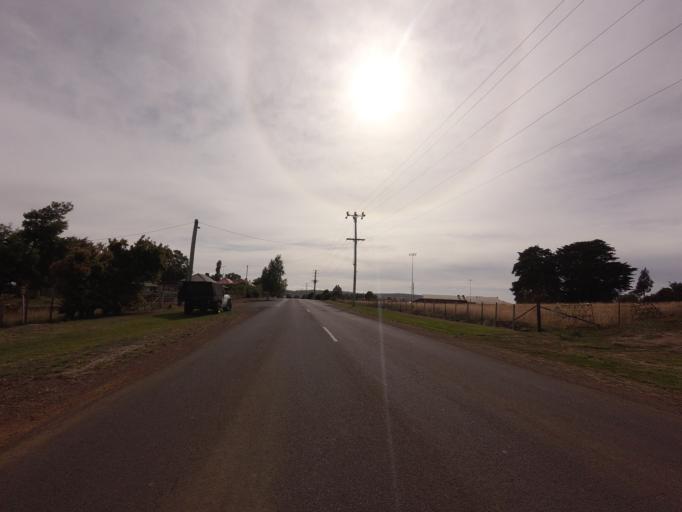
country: AU
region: Tasmania
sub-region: Brighton
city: Bridgewater
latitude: -42.3046
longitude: 147.3642
